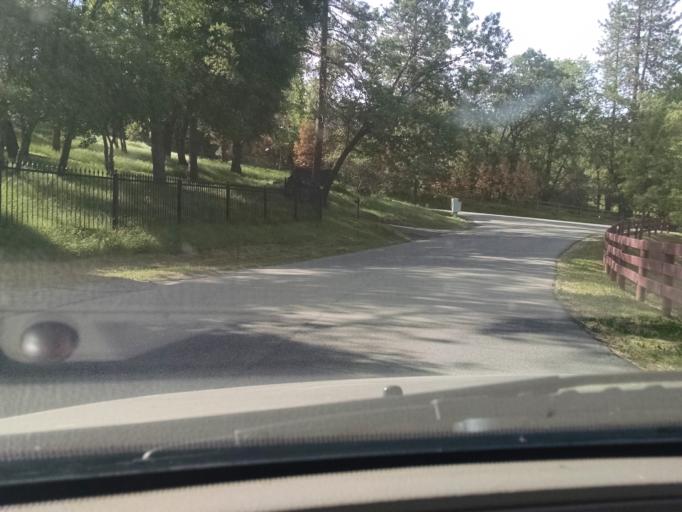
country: US
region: California
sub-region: Madera County
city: Oakhurst
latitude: 37.2924
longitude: -119.6331
